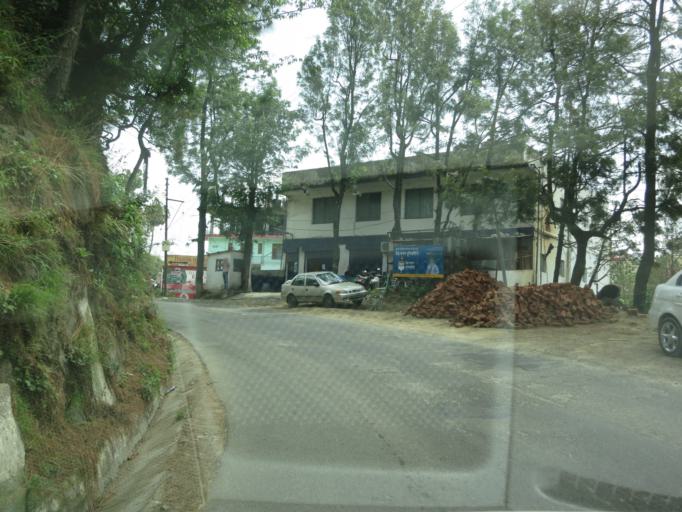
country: IN
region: Himachal Pradesh
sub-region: Solan
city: Dagshai
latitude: 30.8885
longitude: 77.0741
